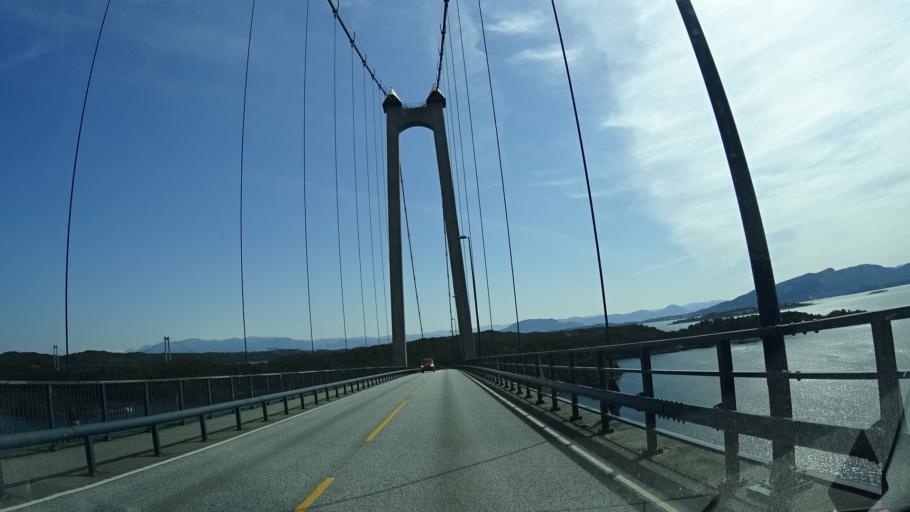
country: NO
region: Hordaland
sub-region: Bomlo
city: Mosterhamn
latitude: 59.7370
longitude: 5.3768
